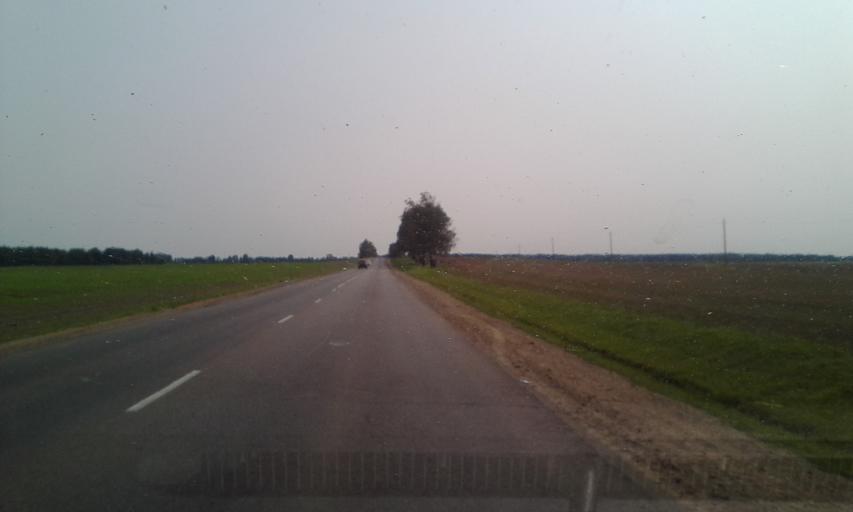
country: BY
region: Minsk
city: Hatava
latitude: 53.8264
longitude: 27.6231
